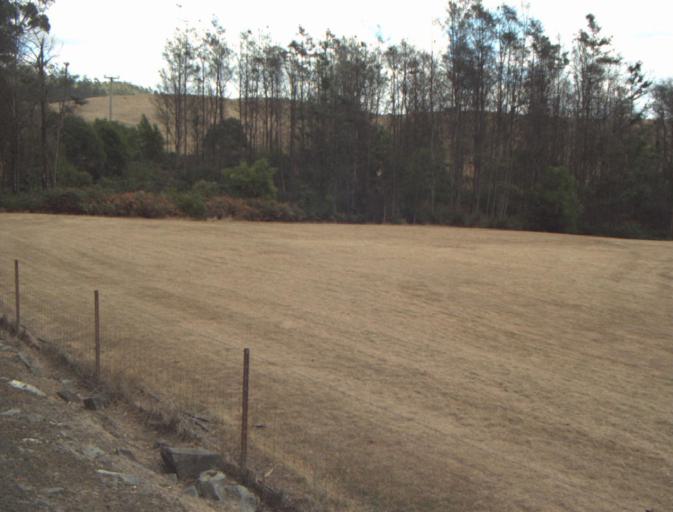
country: AU
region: Tasmania
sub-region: Launceston
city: Mayfield
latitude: -41.1981
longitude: 147.2321
